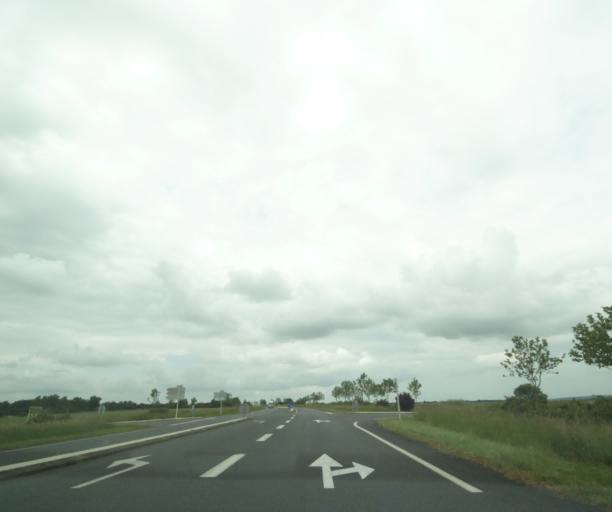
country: FR
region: Poitou-Charentes
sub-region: Departement des Deux-Sevres
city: Saint-Varent
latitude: 46.9012
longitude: -0.1911
